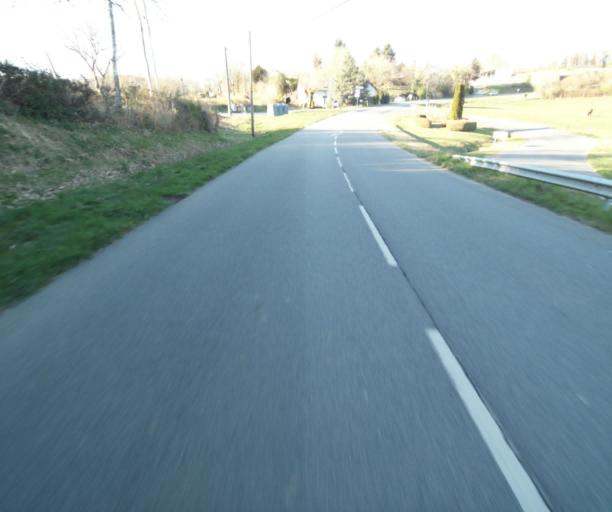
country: FR
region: Limousin
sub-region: Departement de la Correze
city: Saint-Clement
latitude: 45.3439
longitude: 1.6859
